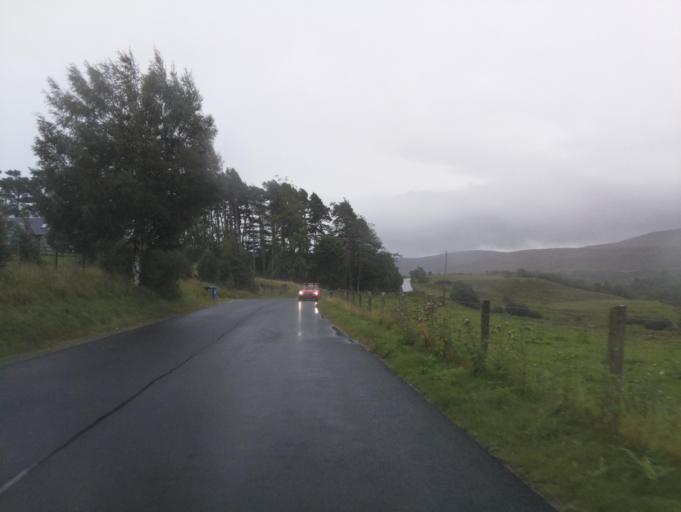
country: GB
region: Scotland
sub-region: Highland
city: Grantown on Spey
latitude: 57.3040
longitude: -3.5697
